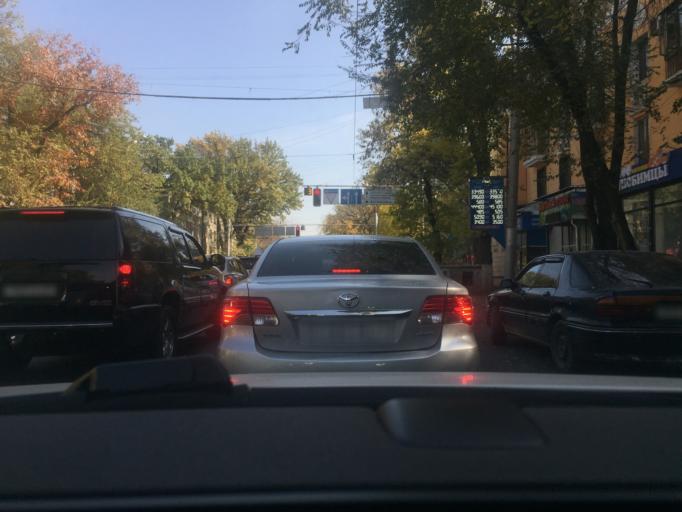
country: KZ
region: Almaty Qalasy
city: Almaty
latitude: 43.2595
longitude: 76.9383
